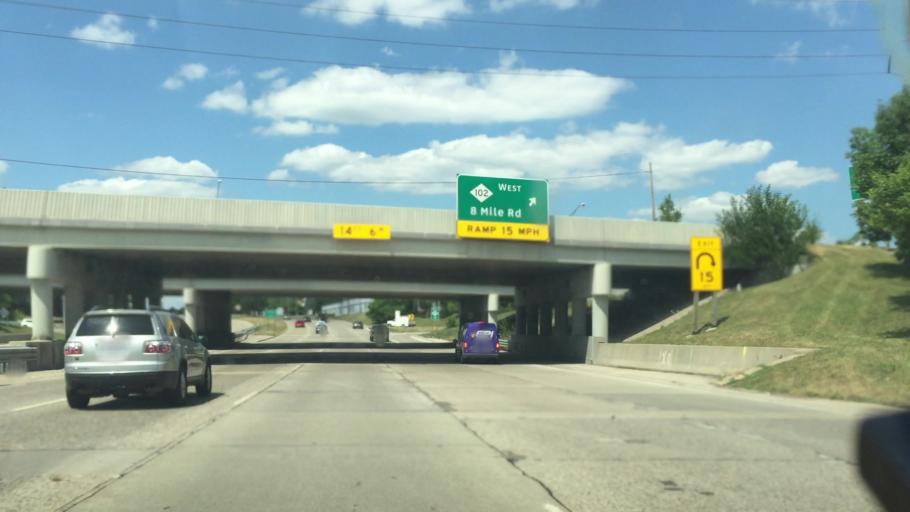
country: US
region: Michigan
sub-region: Wayne County
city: Redford
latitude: 42.4424
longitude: -83.2784
